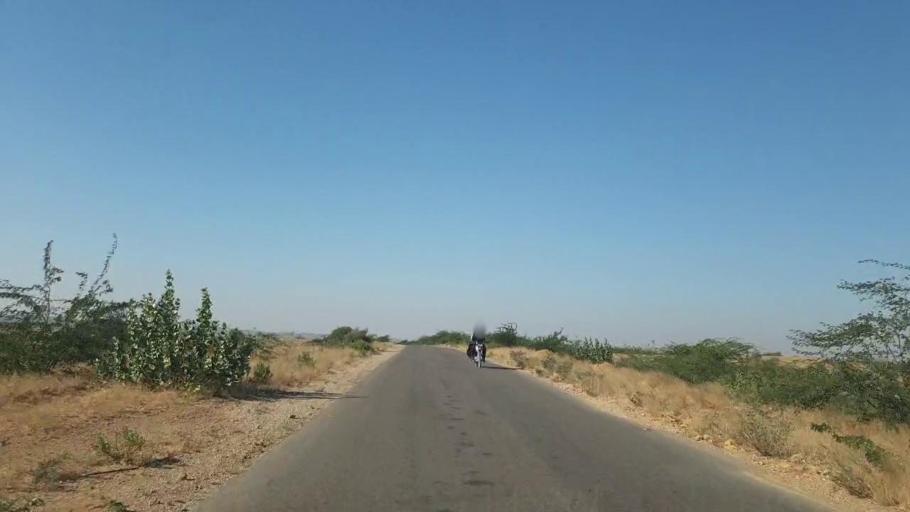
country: PK
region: Sindh
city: Malir Cantonment
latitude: 25.2696
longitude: 67.5937
